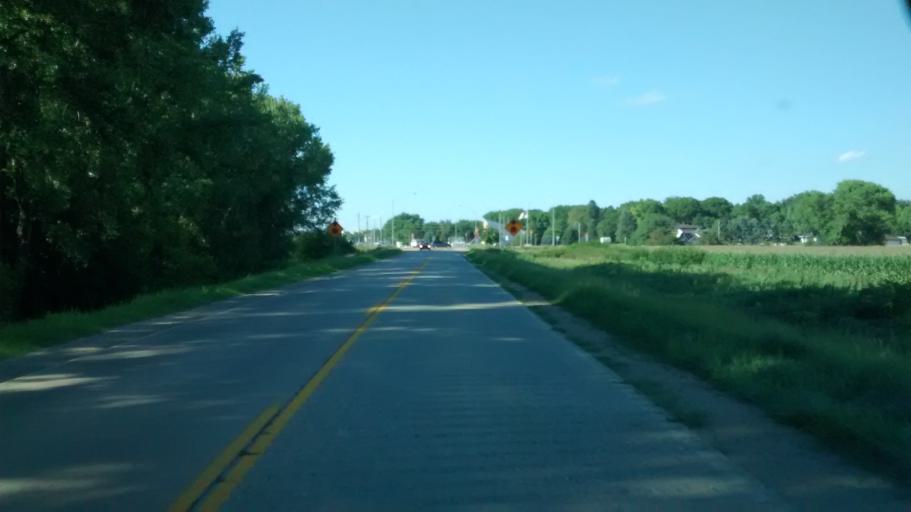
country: US
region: Iowa
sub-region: Woodbury County
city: Moville
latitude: 42.4799
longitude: -96.0761
